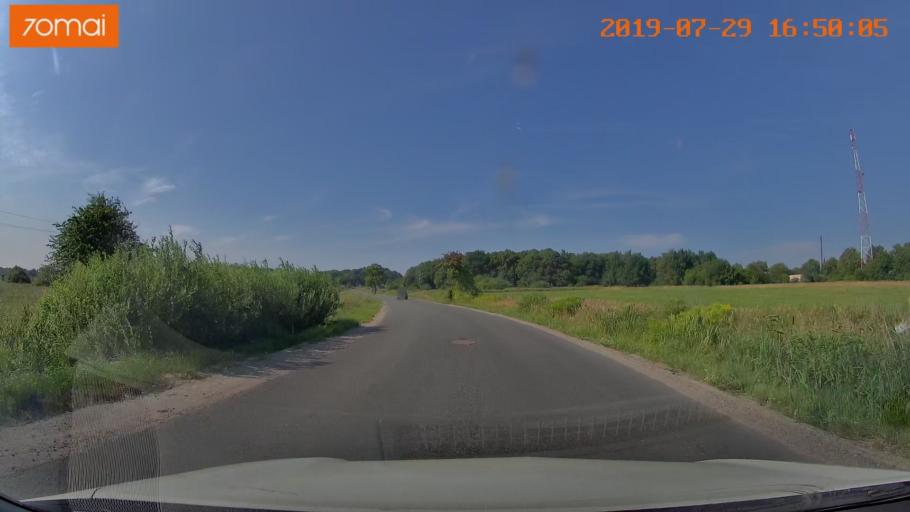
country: RU
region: Kaliningrad
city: Primorsk
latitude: 54.8001
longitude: 20.0580
